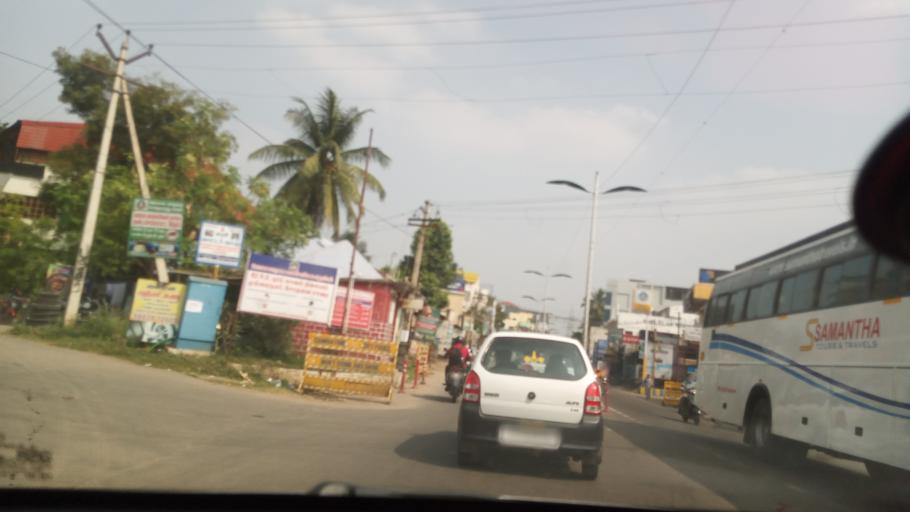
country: IN
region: Tamil Nadu
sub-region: Coimbatore
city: Perur
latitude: 11.0222
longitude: 76.9145
